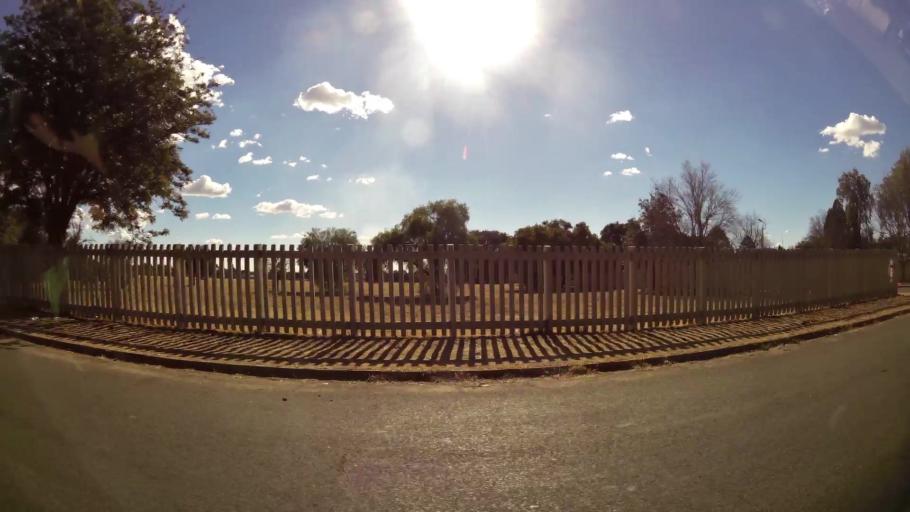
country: ZA
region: North-West
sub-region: Dr Kenneth Kaunda District Municipality
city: Klerksdorp
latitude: -26.8604
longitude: 26.6465
